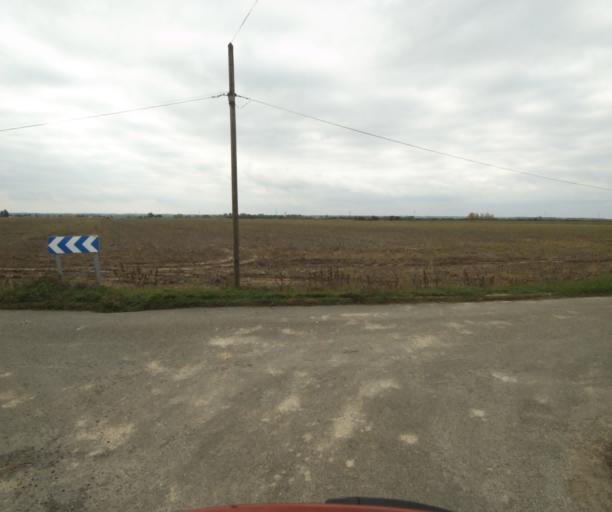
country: FR
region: Midi-Pyrenees
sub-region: Departement du Tarn-et-Garonne
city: Verdun-sur-Garonne
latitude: 43.8896
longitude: 1.2627
